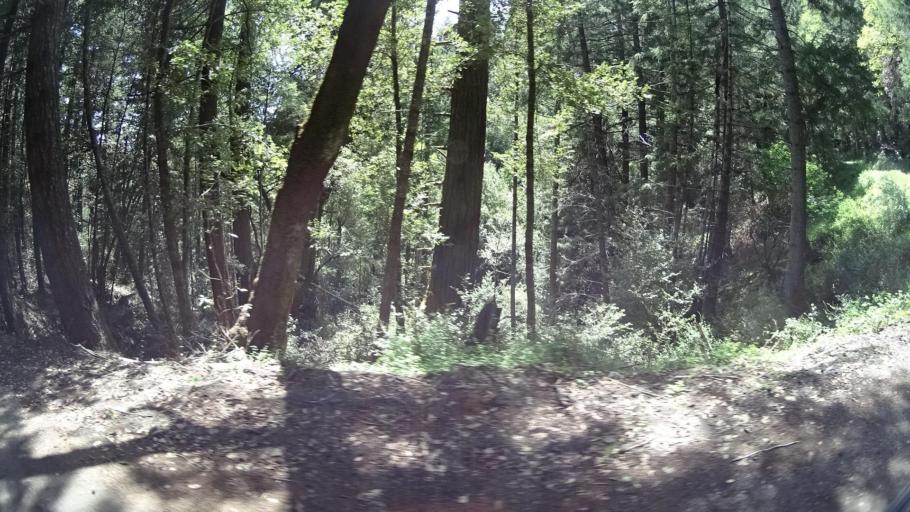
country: US
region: California
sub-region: Humboldt County
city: Redway
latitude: 40.2123
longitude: -123.6646
